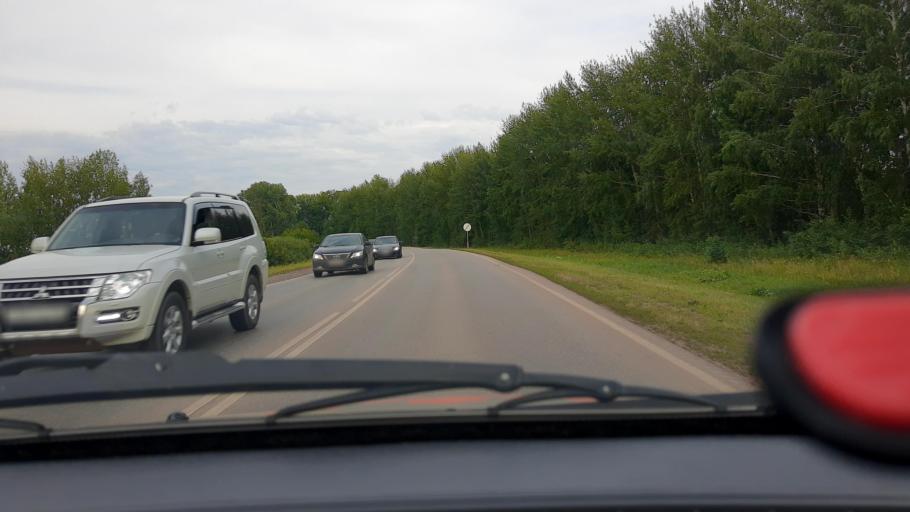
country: RU
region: Bashkortostan
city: Avdon
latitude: 54.5811
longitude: 55.7831
